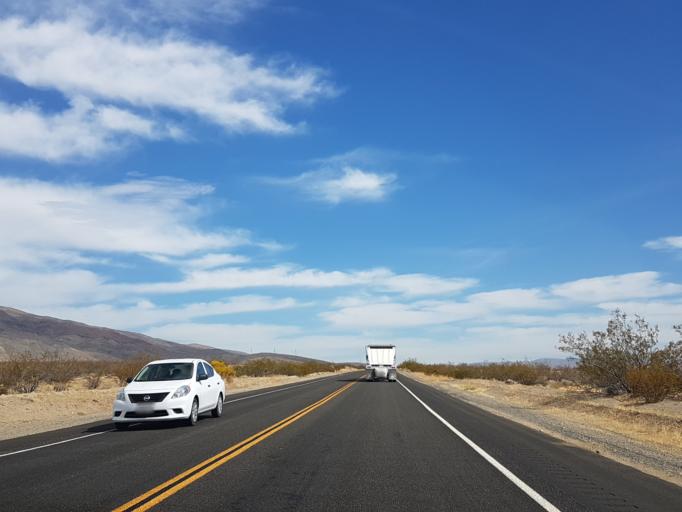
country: US
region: California
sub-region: Kern County
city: Ridgecrest
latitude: 35.4204
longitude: -117.7424
